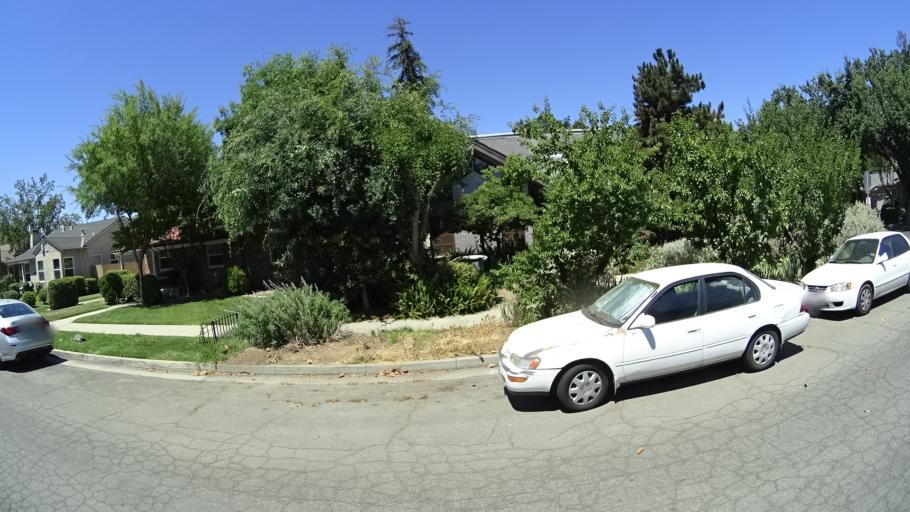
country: US
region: California
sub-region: Fresno County
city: Fresno
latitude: 36.7773
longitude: -119.8108
